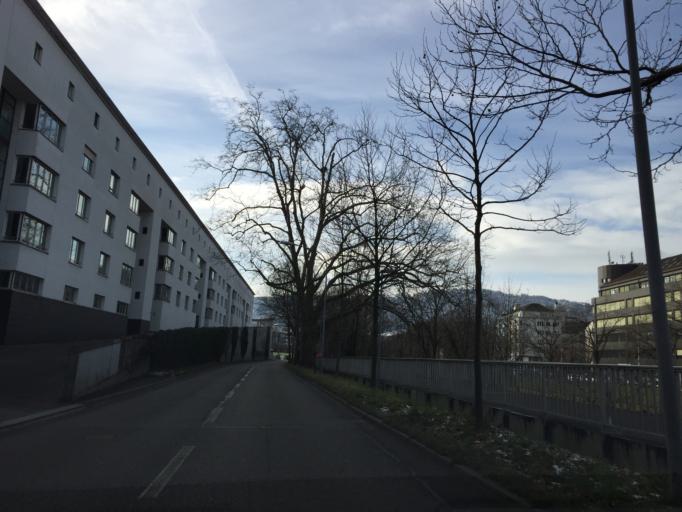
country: CH
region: Zurich
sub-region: Bezirk Zuerich
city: Zuerich (Kreis 1) / City
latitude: 47.3707
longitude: 8.5311
